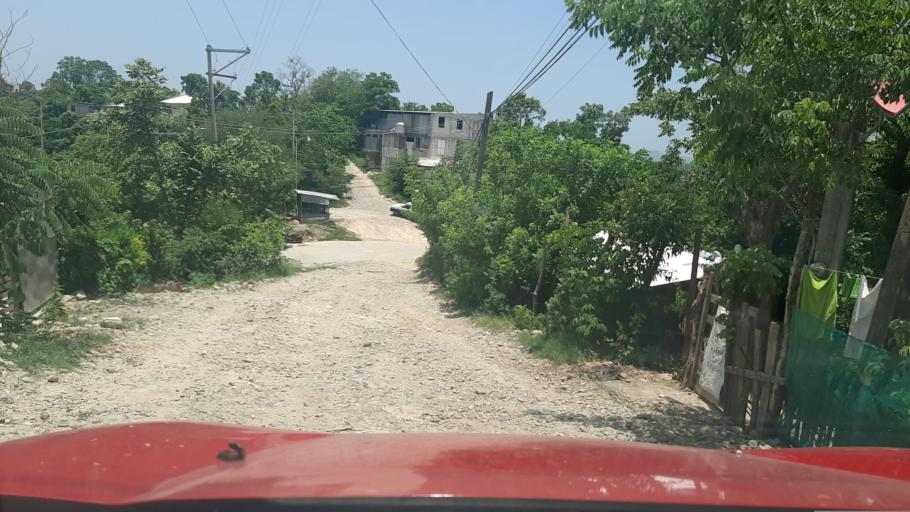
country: MX
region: Veracruz
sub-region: Poza Rica de Hidalgo
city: Arroyo del Maiz Uno
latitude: 20.4985
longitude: -97.4219
